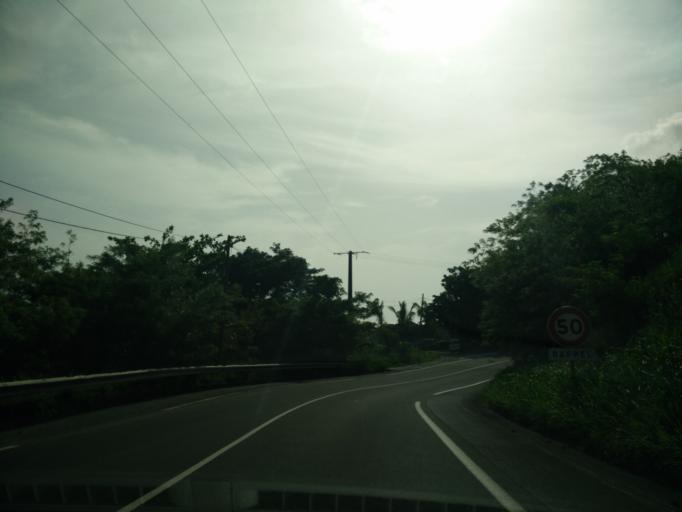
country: MQ
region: Martinique
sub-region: Martinique
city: Saint-Pierre
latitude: 14.7642
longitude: -61.1930
